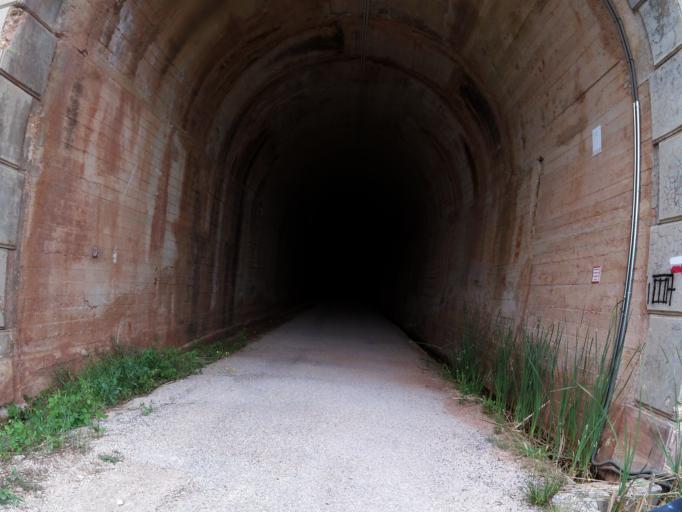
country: ES
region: Castille-La Mancha
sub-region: Provincia de Albacete
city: Alcaraz
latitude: 38.6975
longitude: -2.4810
